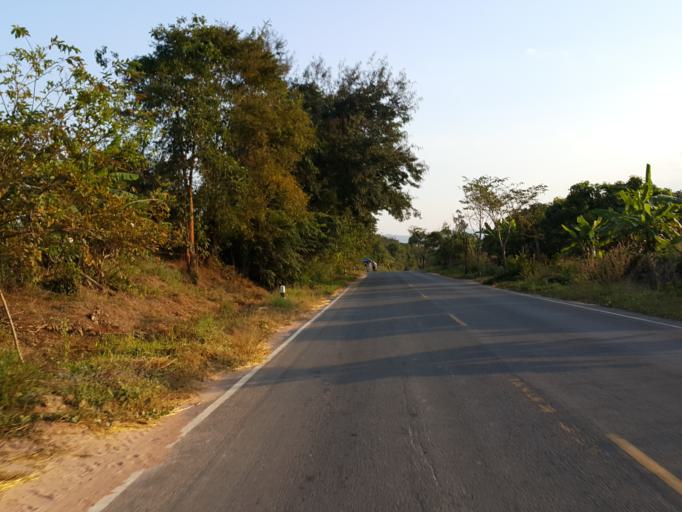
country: TH
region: Lamphun
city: Thung Hua Chang
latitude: 17.8833
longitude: 99.0622
